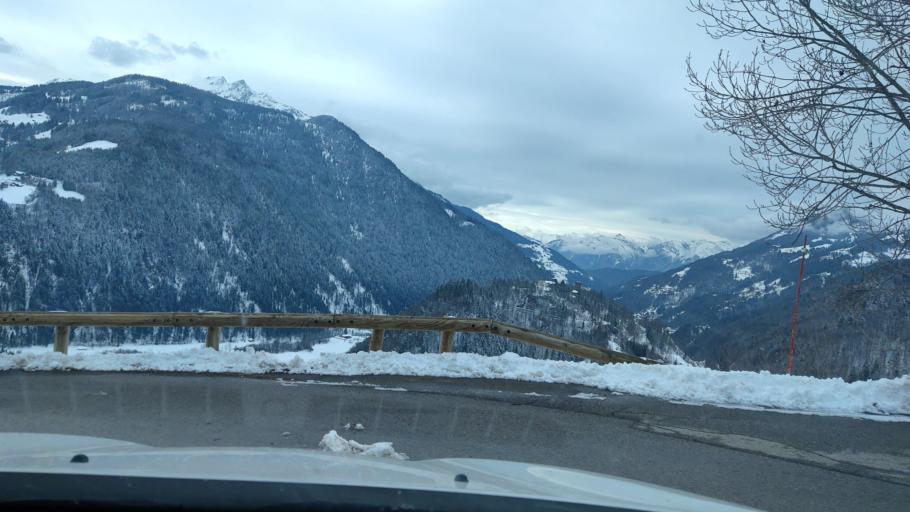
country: FR
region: Rhone-Alpes
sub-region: Departement de la Savoie
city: Beaufort
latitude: 45.7295
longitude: 6.5765
